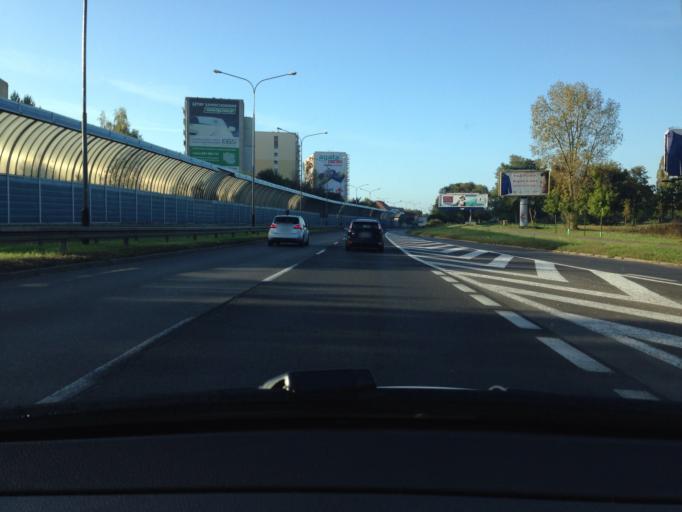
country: PL
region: Greater Poland Voivodeship
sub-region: Poznan
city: Poznan
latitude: 52.4332
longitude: 16.9051
